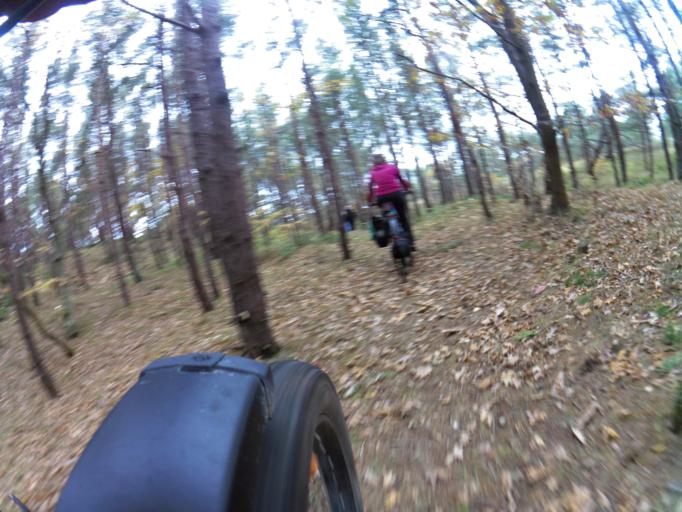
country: PL
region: Pomeranian Voivodeship
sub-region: Powiat pucki
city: Jastarnia
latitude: 54.6985
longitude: 18.6871
